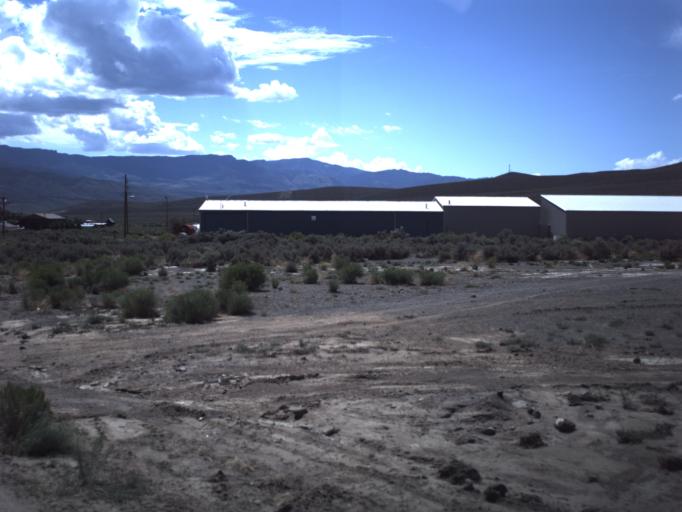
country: US
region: Utah
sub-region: Piute County
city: Junction
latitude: 38.2391
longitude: -112.2280
